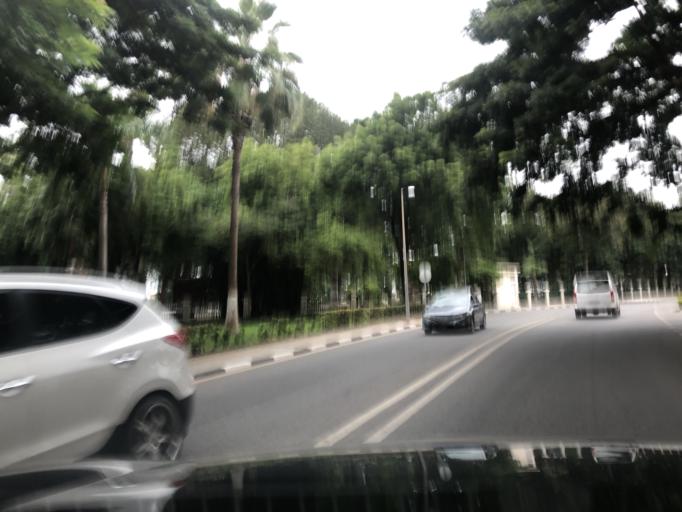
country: AO
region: Luanda
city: Luanda
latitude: -8.8171
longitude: 13.2249
